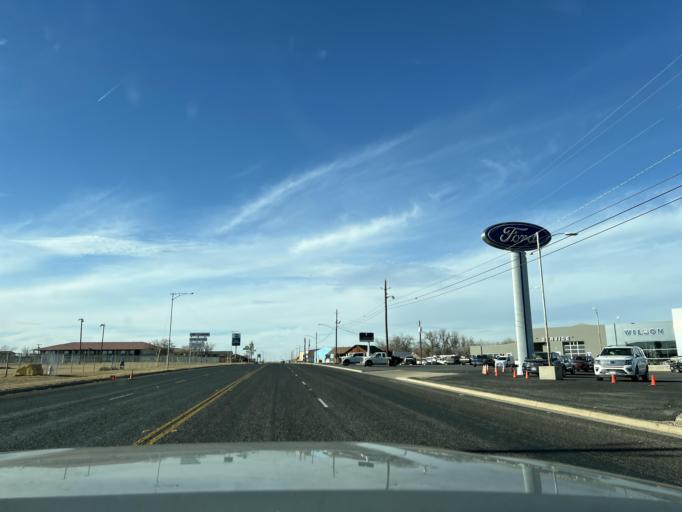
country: US
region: Texas
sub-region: Scurry County
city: Snyder
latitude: 32.7067
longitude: -100.8856
